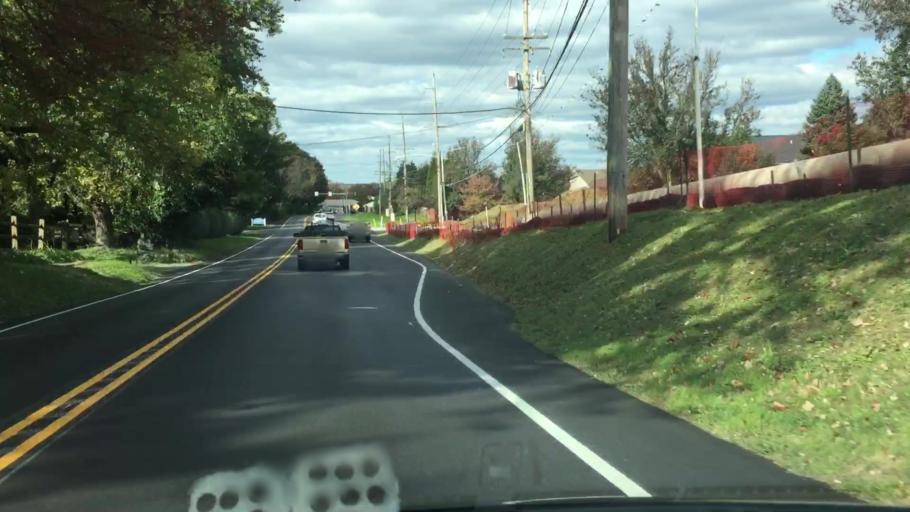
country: US
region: Pennsylvania
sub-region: Chester County
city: Malvern
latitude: 39.9843
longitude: -75.5418
